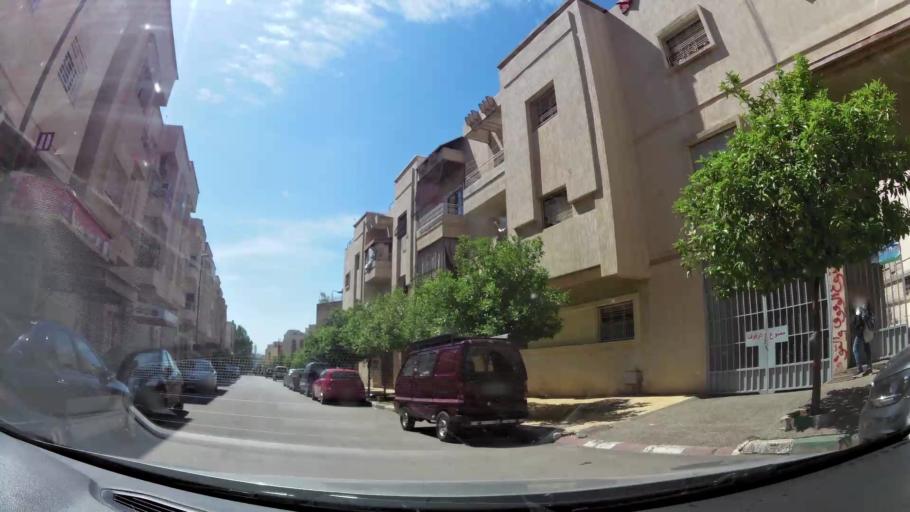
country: MA
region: Fes-Boulemane
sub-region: Fes
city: Fes
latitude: 34.0043
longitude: -4.9788
